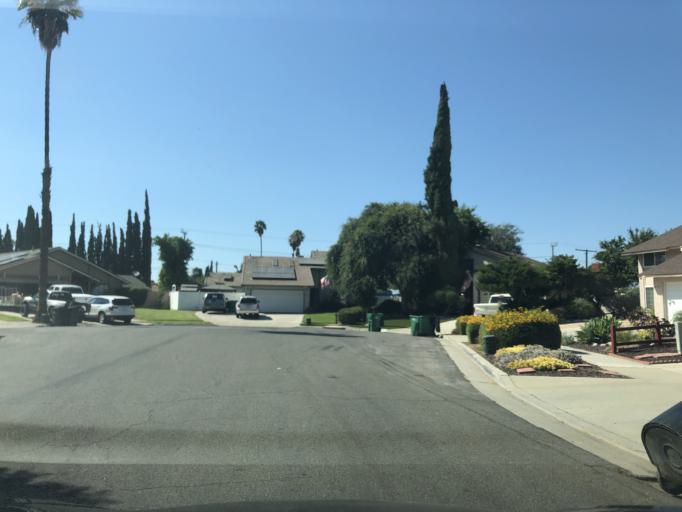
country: US
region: California
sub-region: Riverside County
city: Corona
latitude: 33.8673
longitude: -117.5516
